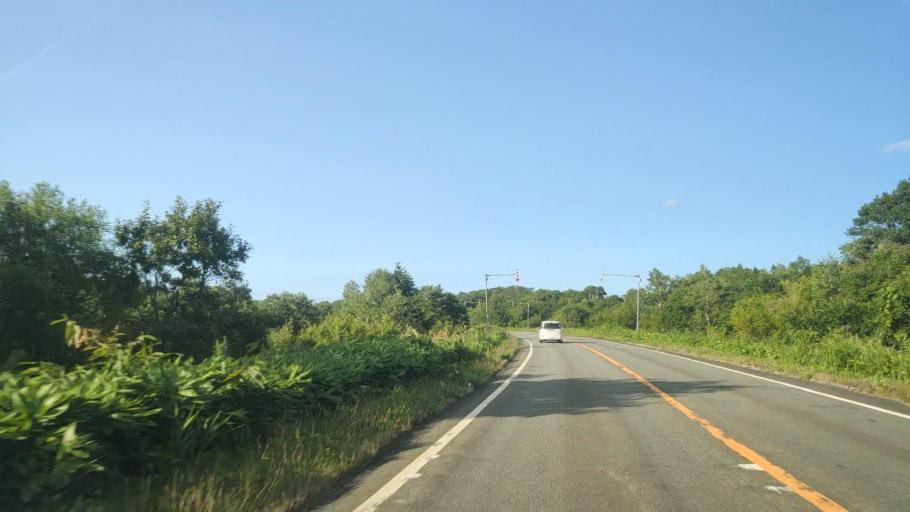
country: JP
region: Hokkaido
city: Makubetsu
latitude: 45.0729
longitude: 141.7528
